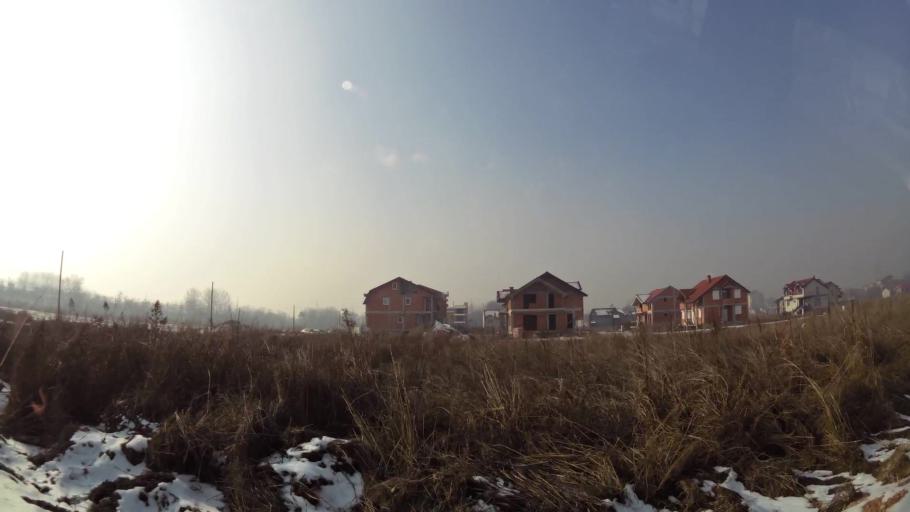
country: MK
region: Kisela Voda
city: Kisela Voda
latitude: 41.9922
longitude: 21.5171
